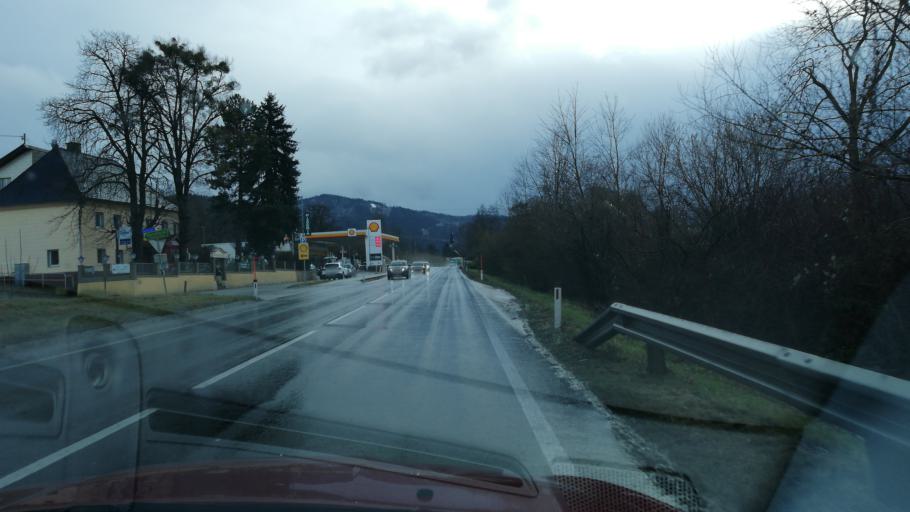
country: AT
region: Upper Austria
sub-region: Politischer Bezirk Kirchdorf an der Krems
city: Micheldorf in Oberoesterreich
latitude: 47.9126
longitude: 14.1133
